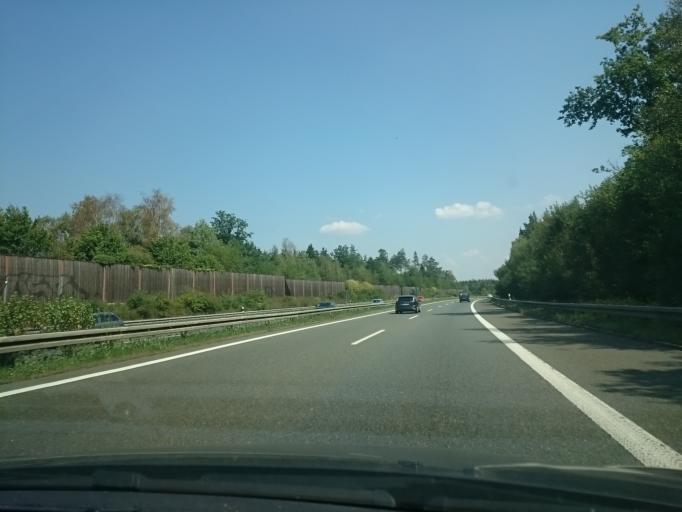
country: DE
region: Saxony
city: Hirschfeld
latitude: 50.6471
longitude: 12.4565
